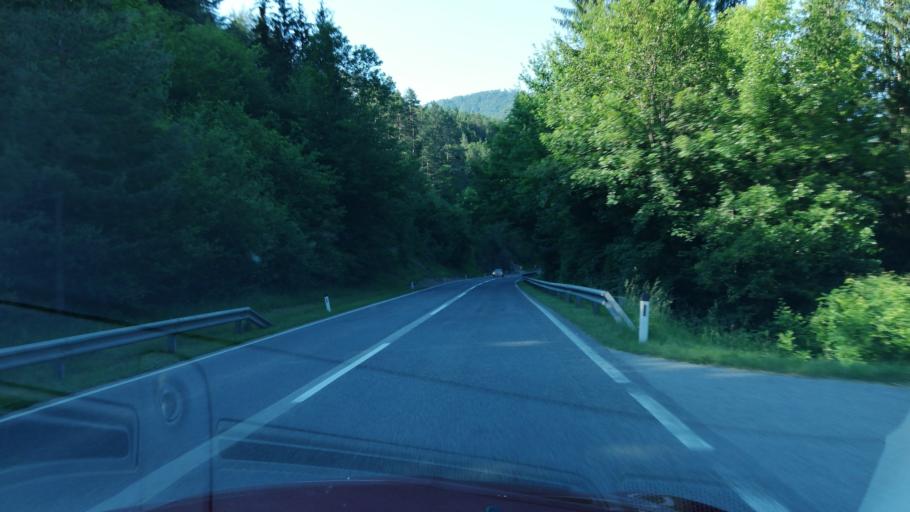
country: AT
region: Upper Austria
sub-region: Politischer Bezirk Kirchdorf an der Krems
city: Micheldorf in Oberoesterreich
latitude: 47.8608
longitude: 14.1930
